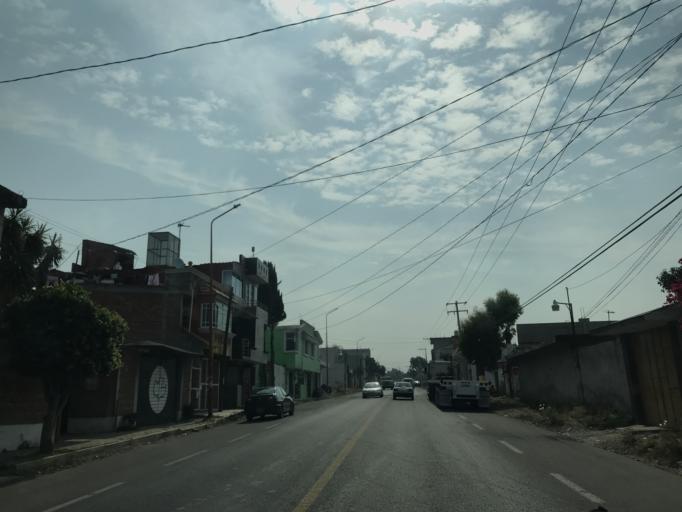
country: MX
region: Tlaxcala
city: Tenancingo
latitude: 19.1513
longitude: -98.2134
